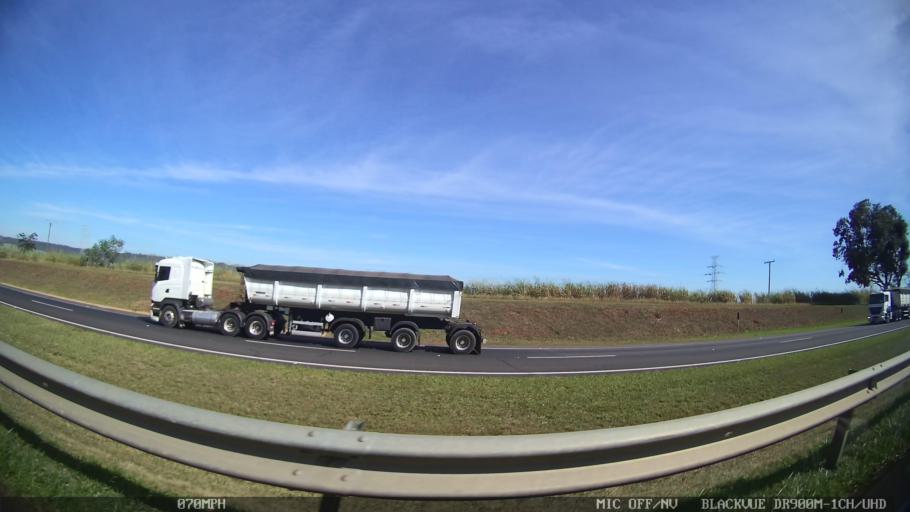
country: BR
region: Sao Paulo
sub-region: Pirassununga
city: Pirassununga
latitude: -21.9802
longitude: -47.4518
